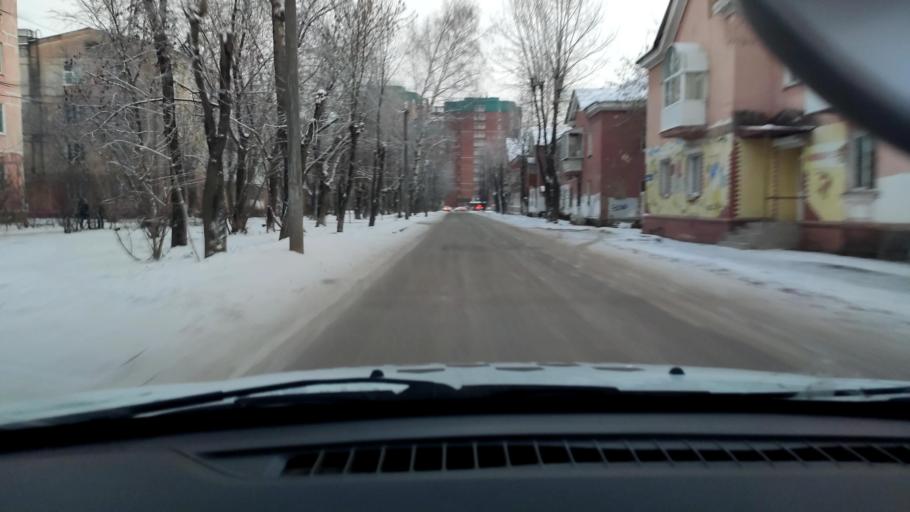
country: RU
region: Perm
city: Kultayevo
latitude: 58.0053
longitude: 55.9624
